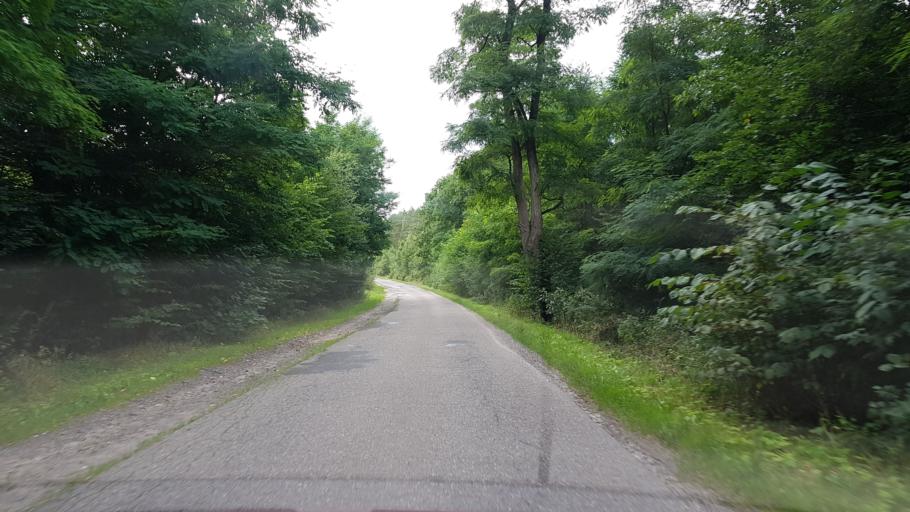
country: PL
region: West Pomeranian Voivodeship
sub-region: Powiat bialogardzki
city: Tychowo
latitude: 54.0280
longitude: 16.3540
